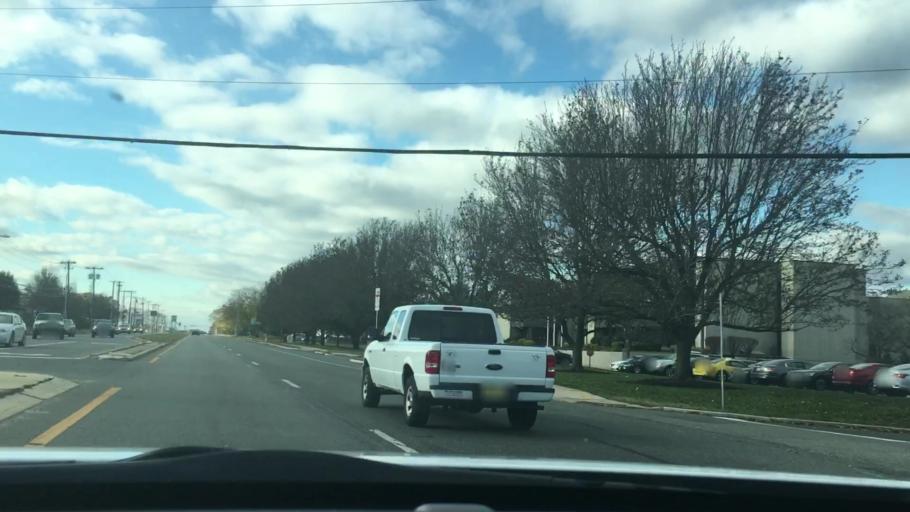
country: US
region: New Jersey
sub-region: Atlantic County
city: Pleasantville
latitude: 39.3955
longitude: -74.5443
